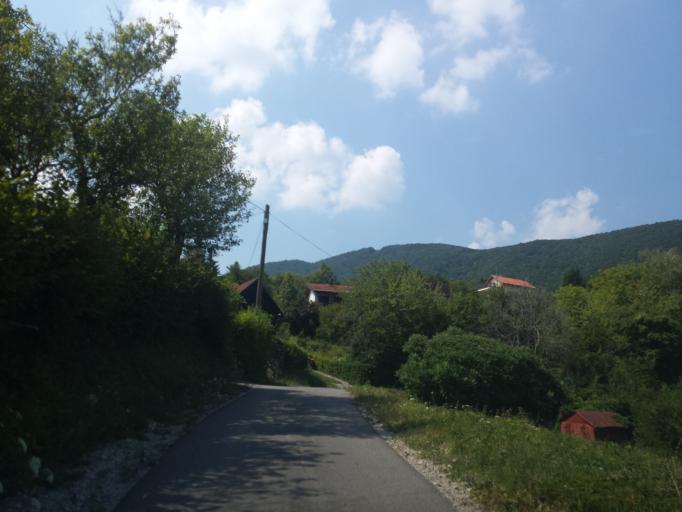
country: HR
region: Zagrebacka
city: Rude
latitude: 45.7261
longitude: 15.6806
